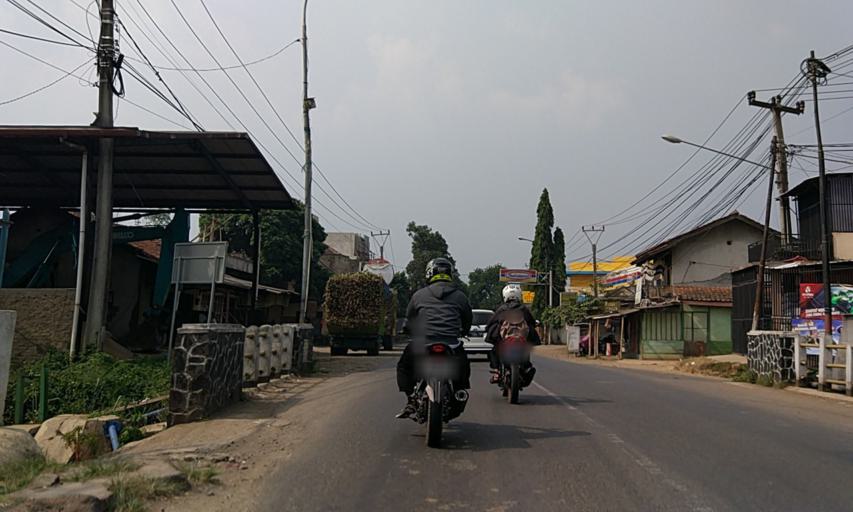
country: ID
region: West Java
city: Banjaran
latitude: -7.0516
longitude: 107.5760
